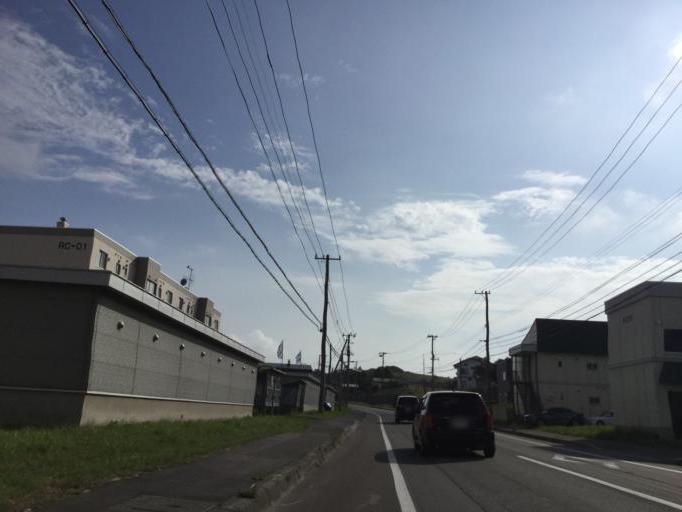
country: JP
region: Hokkaido
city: Wakkanai
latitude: 45.3865
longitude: 141.6745
